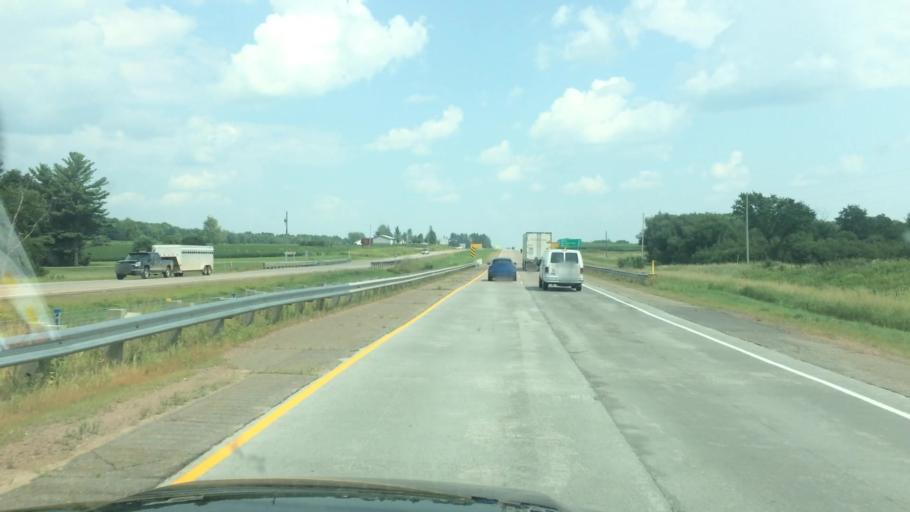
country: US
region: Wisconsin
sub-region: Clark County
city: Abbotsford
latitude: 44.9457
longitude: -90.2788
